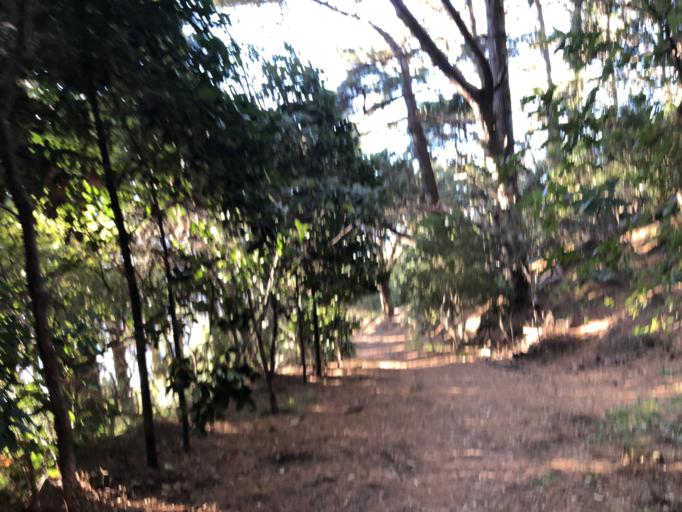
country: NZ
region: Wellington
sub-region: Wellington City
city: Wellington
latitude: -41.2999
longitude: 174.7886
